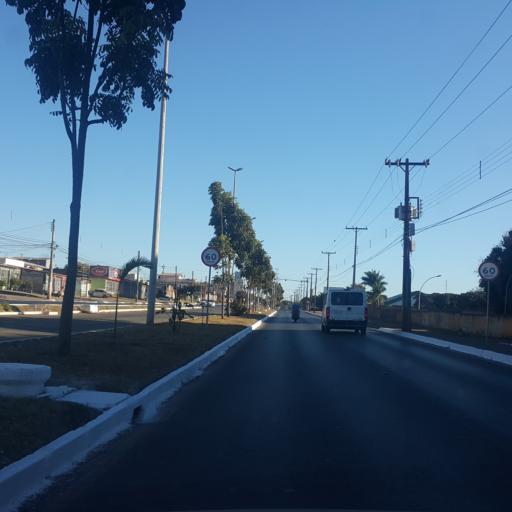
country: BR
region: Federal District
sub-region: Brasilia
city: Brasilia
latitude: -15.8216
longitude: -48.0946
